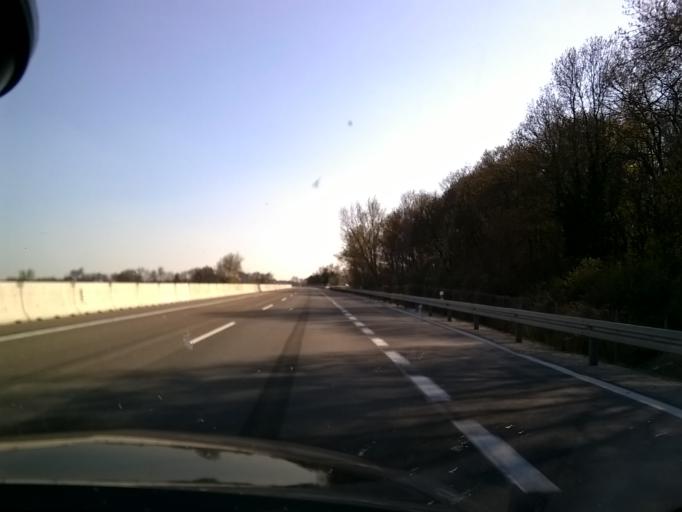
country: SK
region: Trnavsky
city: Leopoldov
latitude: 48.4557
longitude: 17.7391
